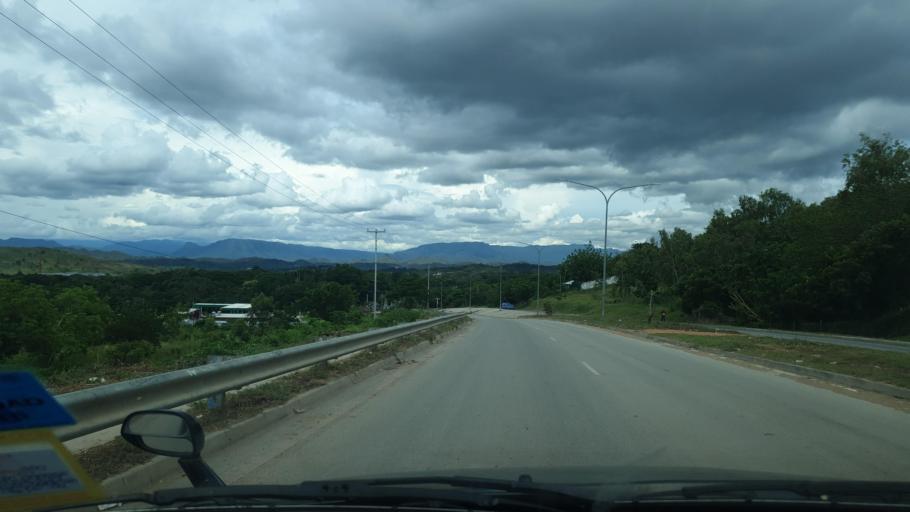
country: PG
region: National Capital
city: Port Moresby
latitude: -9.4086
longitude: 147.1612
